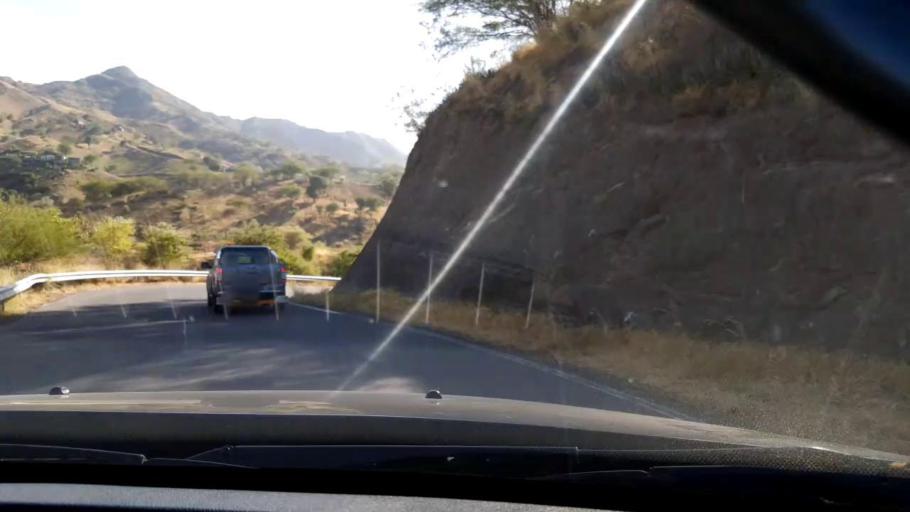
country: CV
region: Sao Lourenco dos Orgaos
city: Joao Teves
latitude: 15.0718
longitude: -23.5695
